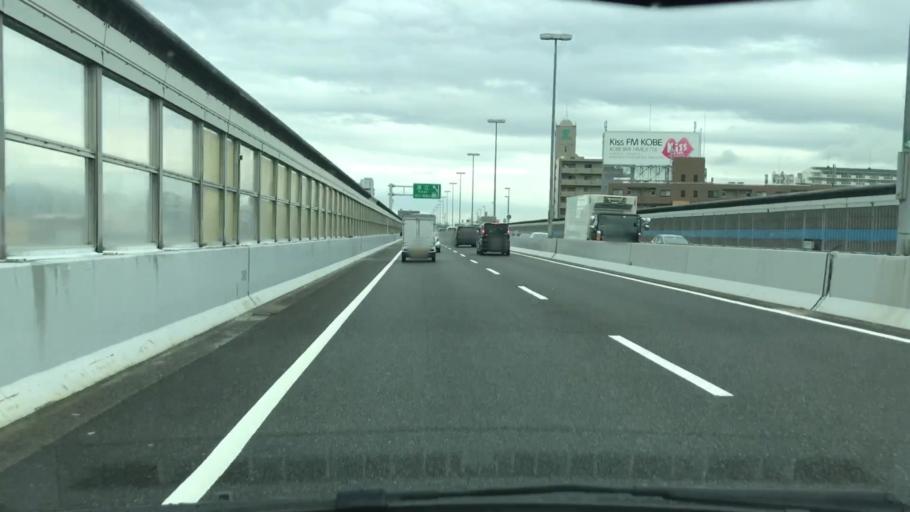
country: JP
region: Hyogo
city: Ashiya
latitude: 34.7157
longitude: 135.2816
